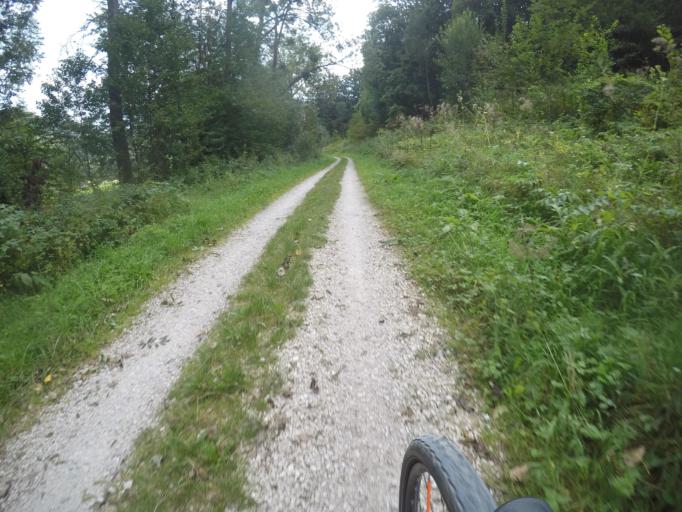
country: DE
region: Baden-Wuerttemberg
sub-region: Tuebingen Region
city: Bad Urach
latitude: 48.4712
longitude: 9.4158
